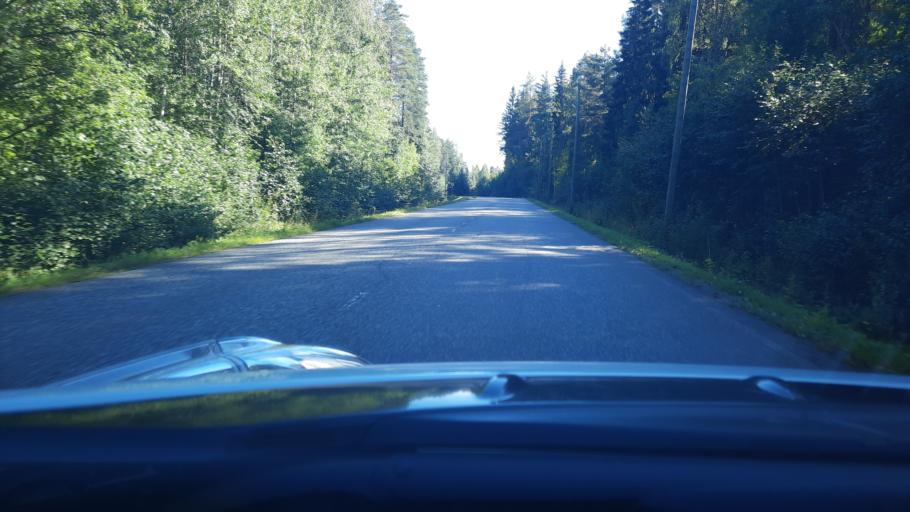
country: FI
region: North Karelia
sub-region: Joensuu
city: Joensuu
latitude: 62.6349
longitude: 29.6995
